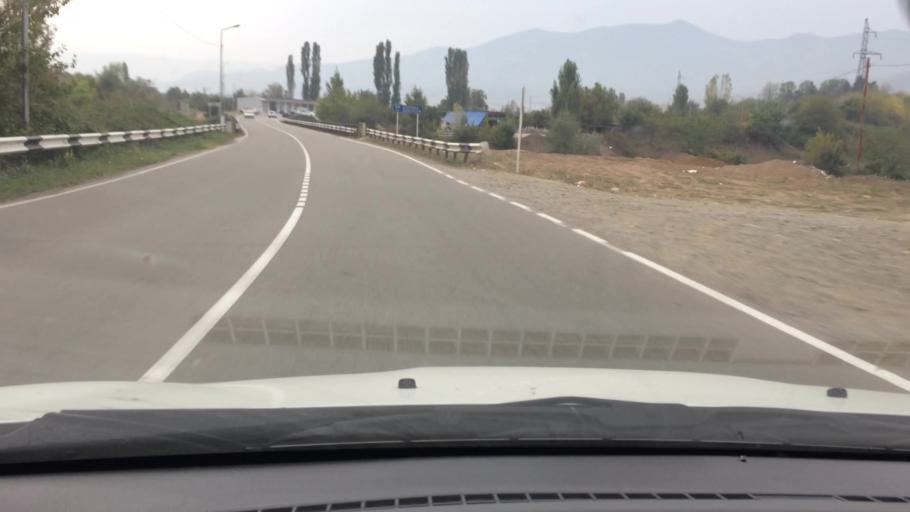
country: AM
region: Tavush
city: Bagratashen
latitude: 41.2560
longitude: 44.7981
